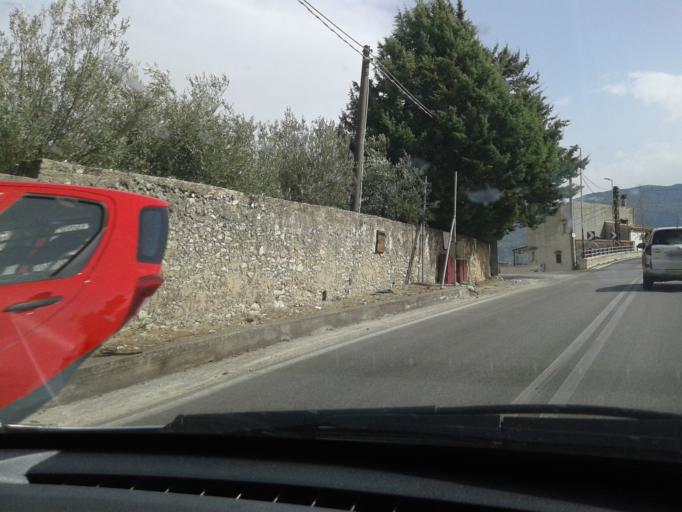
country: IT
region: Sicily
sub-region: Palermo
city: Cannizzaro-Favara
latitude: 38.0688
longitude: 13.2692
